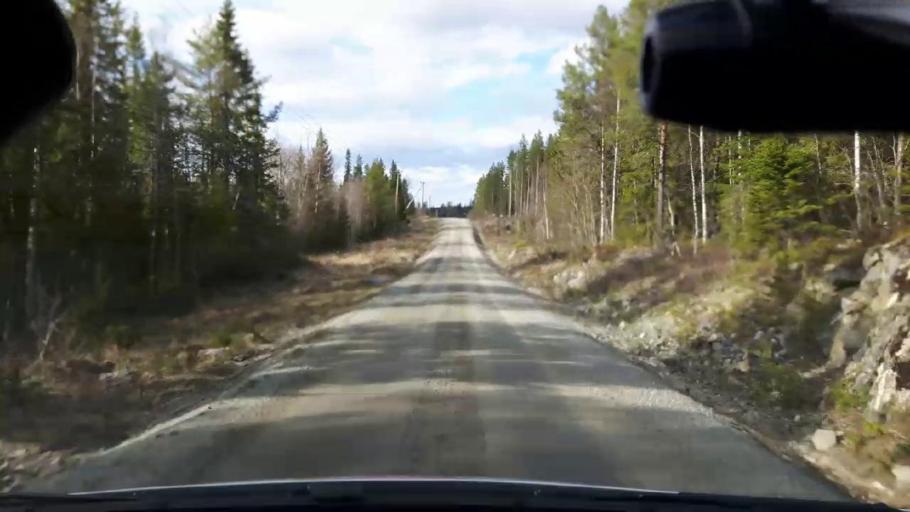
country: SE
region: Jaemtland
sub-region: Bergs Kommun
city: Hoverberg
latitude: 62.8737
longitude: 14.6667
